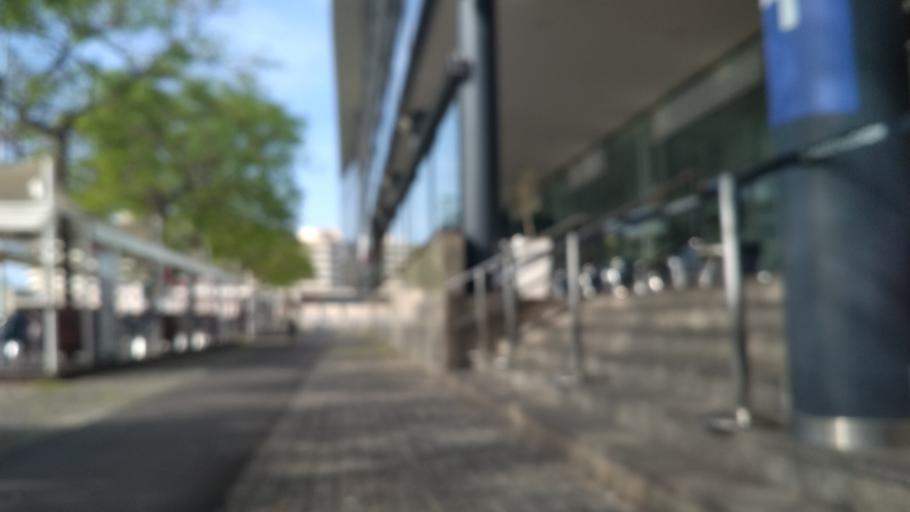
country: ES
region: Catalonia
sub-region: Provincia de Barcelona
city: Ciutat Vella
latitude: 41.3751
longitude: 2.1835
